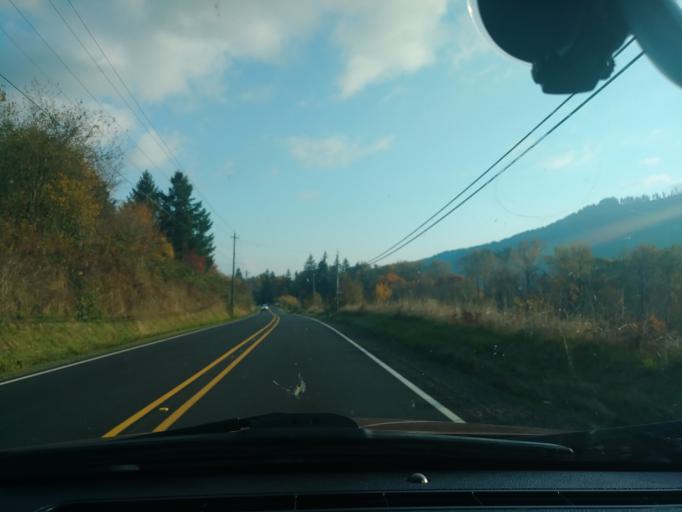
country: US
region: Oregon
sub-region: Washington County
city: Forest Grove
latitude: 45.5612
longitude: -123.1904
